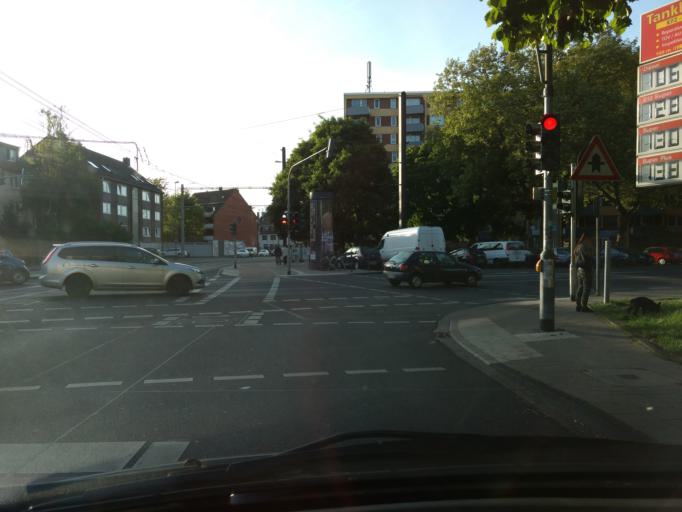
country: DE
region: North Rhine-Westphalia
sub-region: Regierungsbezirk Koln
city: Bilderstoeckchen
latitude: 50.9652
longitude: 6.9123
